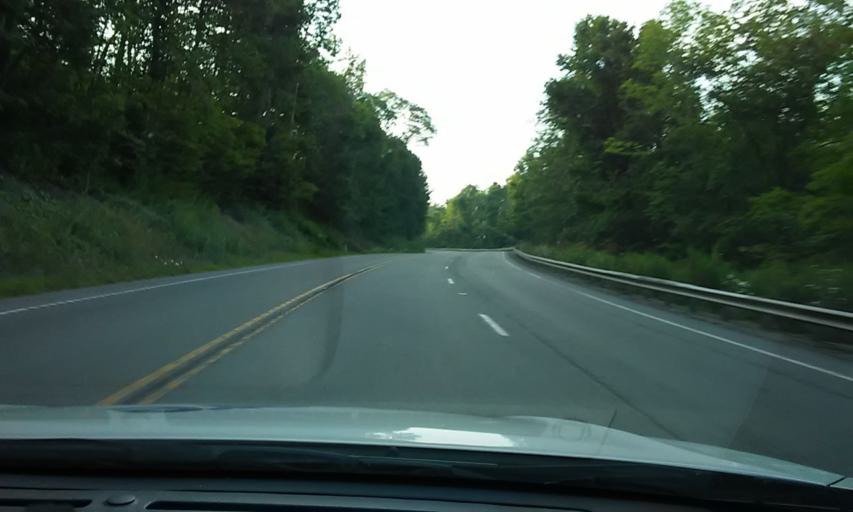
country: US
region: Pennsylvania
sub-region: McKean County
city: Smethport
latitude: 41.7103
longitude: -78.5962
